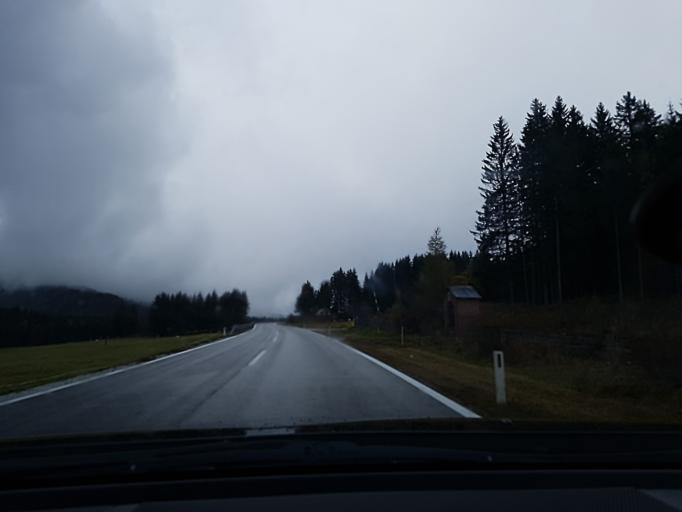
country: AT
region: Styria
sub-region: Politischer Bezirk Murtal
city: Hohentauern
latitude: 47.3987
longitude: 14.4645
